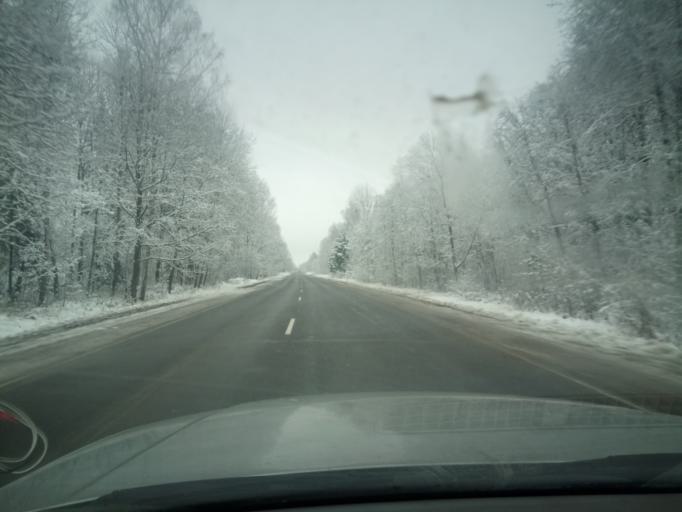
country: BY
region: Vitebsk
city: Syanno
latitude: 54.9704
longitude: 29.8761
